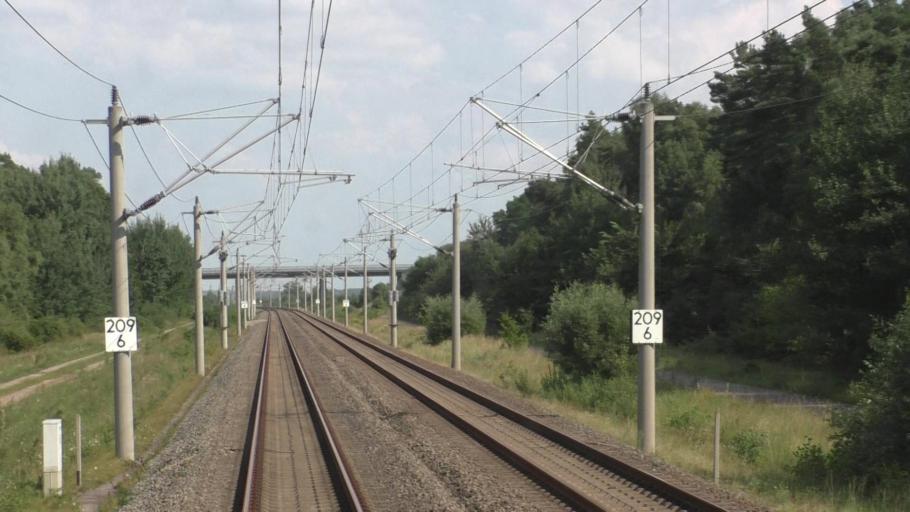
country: DE
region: Saxony-Anhalt
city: Uenglingen
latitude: 52.5780
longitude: 11.7975
